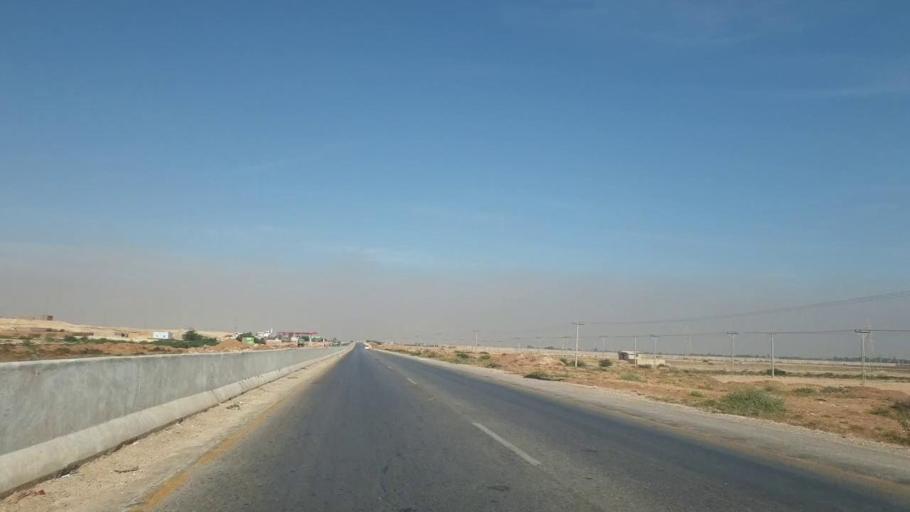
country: PK
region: Sindh
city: Jamshoro
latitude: 25.4953
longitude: 68.2723
